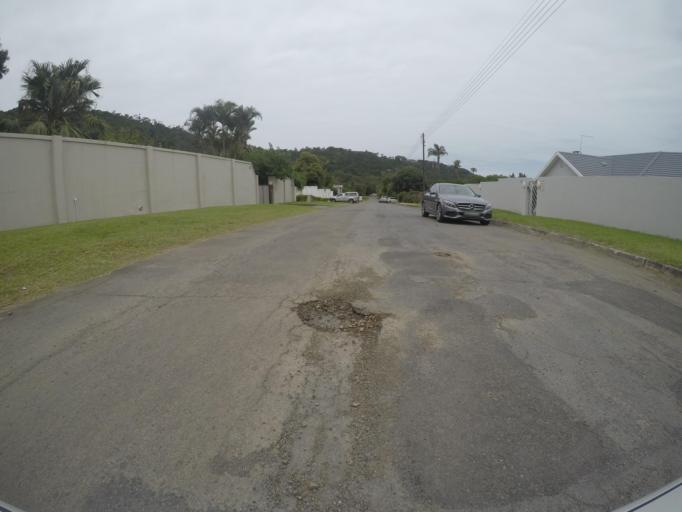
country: ZA
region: Eastern Cape
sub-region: Buffalo City Metropolitan Municipality
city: East London
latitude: -32.9713
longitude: 27.9315
